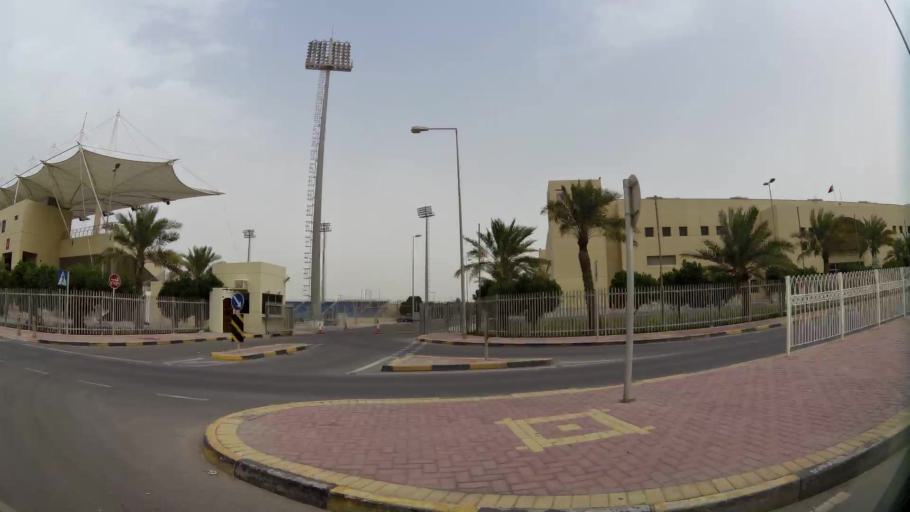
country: BH
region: Northern
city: Madinat `Isa
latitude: 26.1737
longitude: 50.5482
